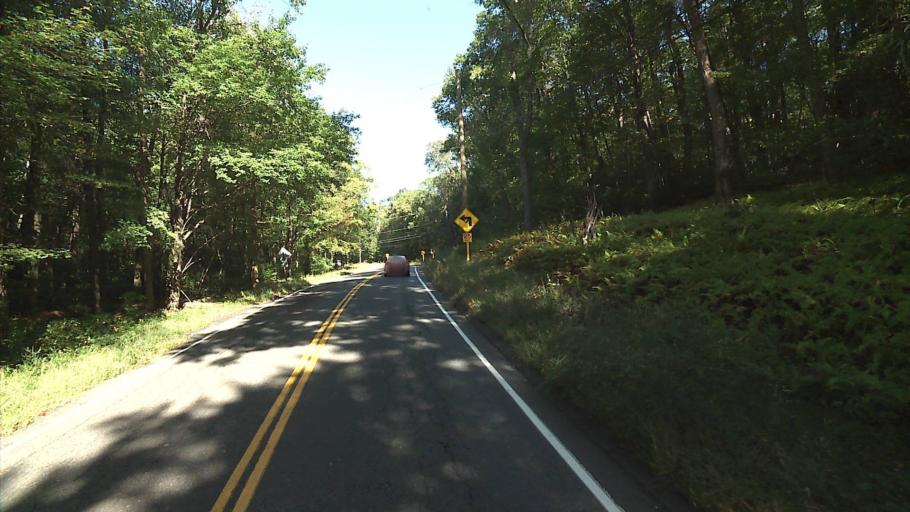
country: US
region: Connecticut
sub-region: Hartford County
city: Bristol
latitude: 41.7319
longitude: -72.9528
